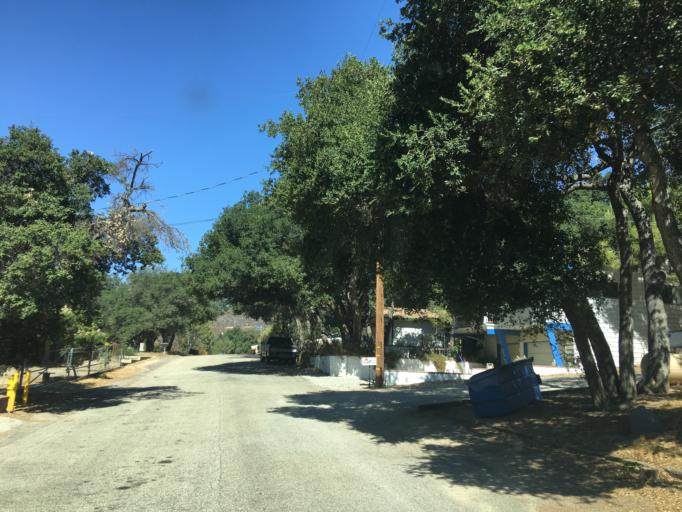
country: US
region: California
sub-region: Los Angeles County
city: Green Valley
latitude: 34.6190
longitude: -118.4165
